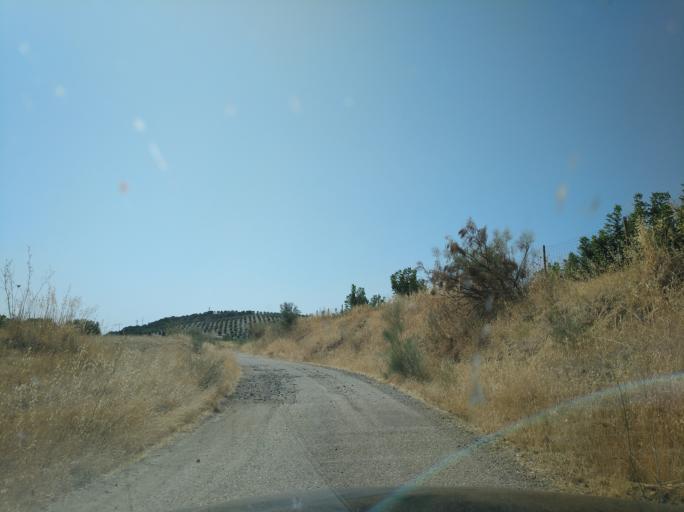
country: PT
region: Portalegre
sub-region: Campo Maior
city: Campo Maior
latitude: 39.0645
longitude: -7.0124
